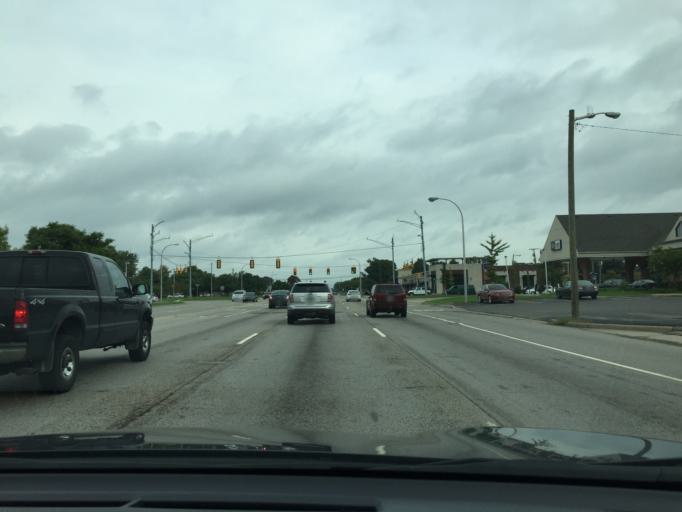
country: US
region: Michigan
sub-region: Oakland County
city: Southfield
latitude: 42.4724
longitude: -83.2211
